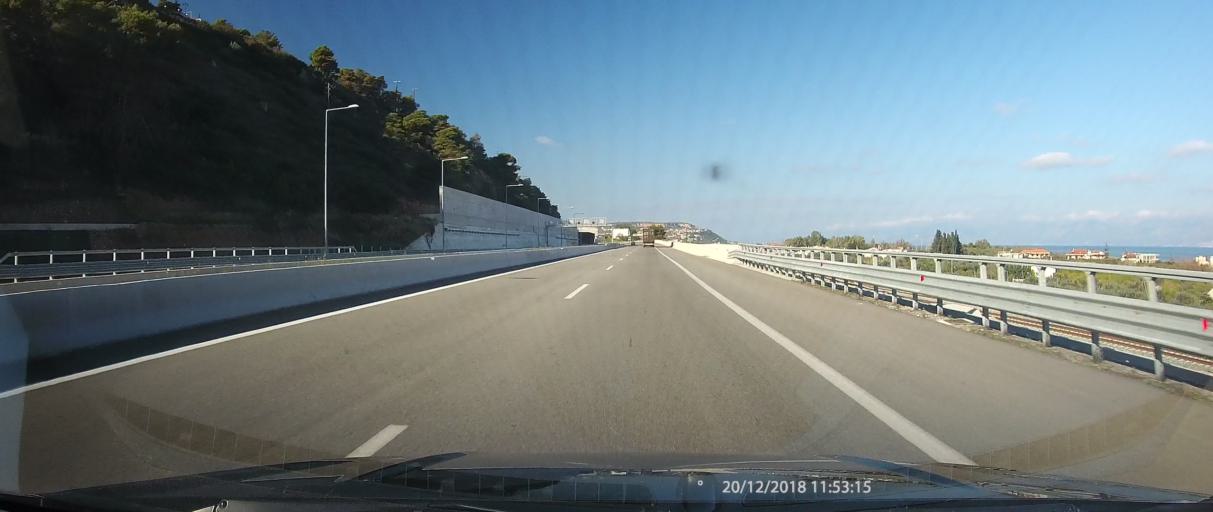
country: GR
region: West Greece
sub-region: Nomos Achaias
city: Aiyira
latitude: 38.1427
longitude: 22.3683
